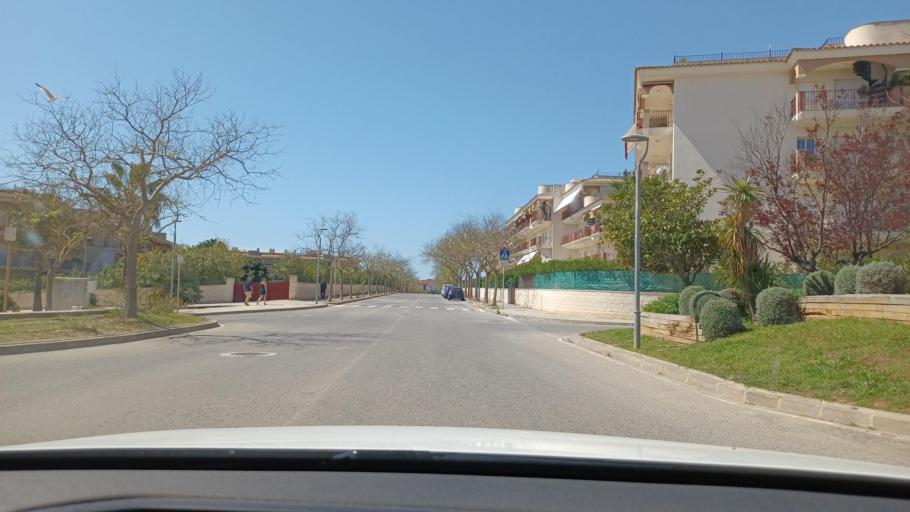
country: ES
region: Catalonia
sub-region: Provincia de Tarragona
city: Sant Carles de la Rapita
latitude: 40.6097
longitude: 0.5814
